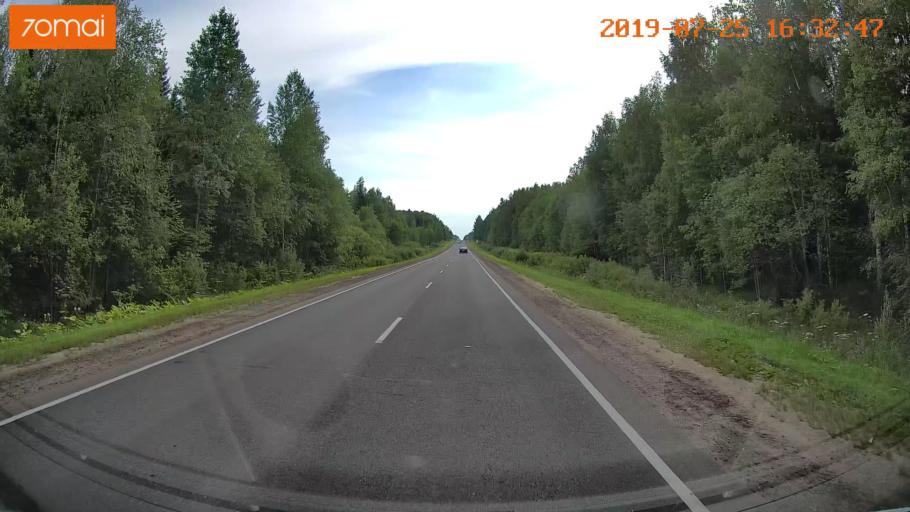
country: RU
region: Ivanovo
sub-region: Privolzhskiy Rayon
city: Ples
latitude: 57.4336
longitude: 41.4686
